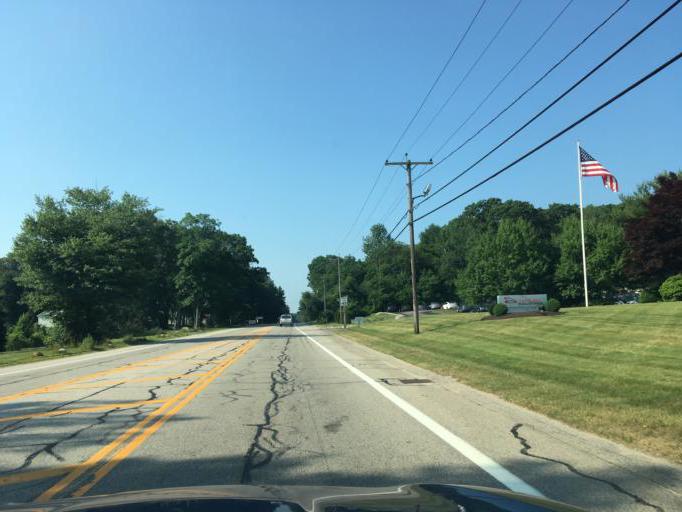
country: US
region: Rhode Island
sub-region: Washington County
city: Kingston
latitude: 41.5216
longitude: -71.5539
